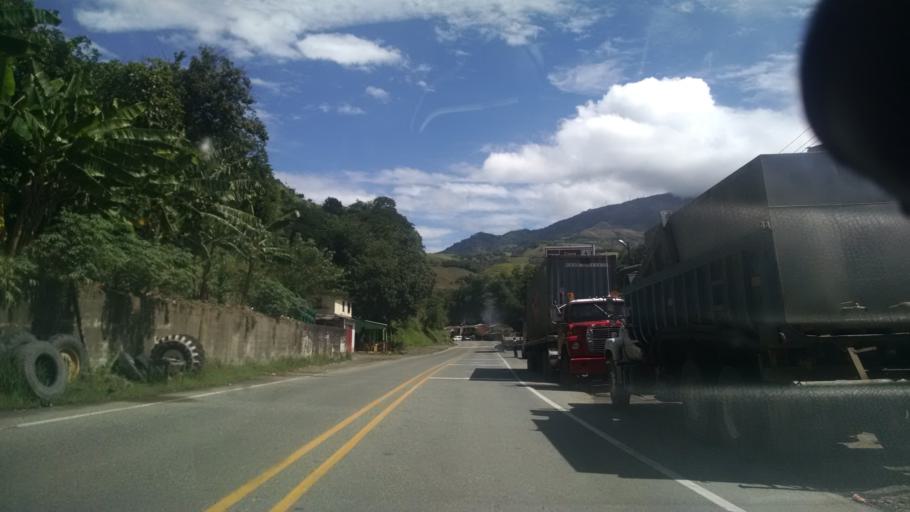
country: CO
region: Caldas
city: Supia
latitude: 5.3864
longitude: -75.6023
